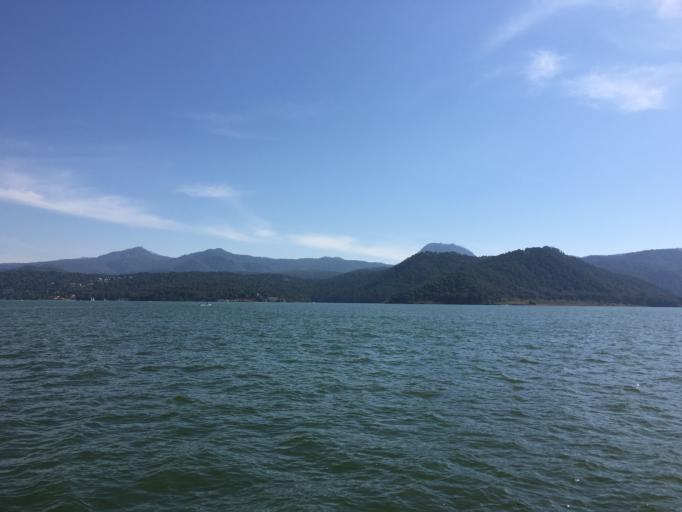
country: MX
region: Mexico
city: Valle de Bravo
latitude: 19.1963
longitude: -100.1514
